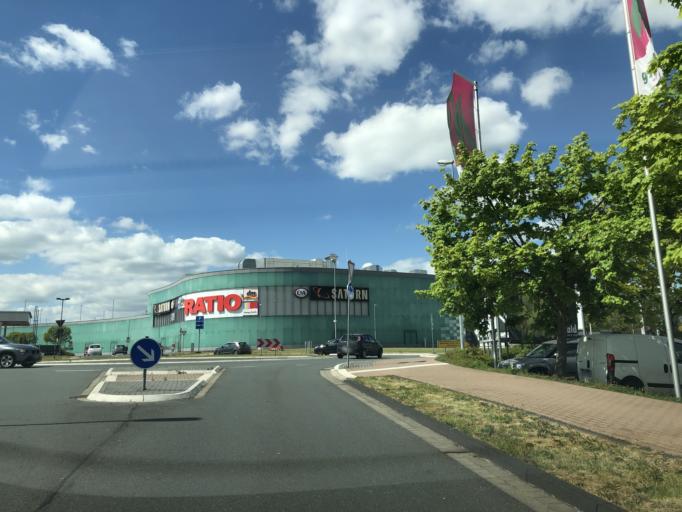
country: DE
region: Hesse
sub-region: Regierungsbezirk Kassel
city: Baunatal
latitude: 51.2271
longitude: 9.4309
